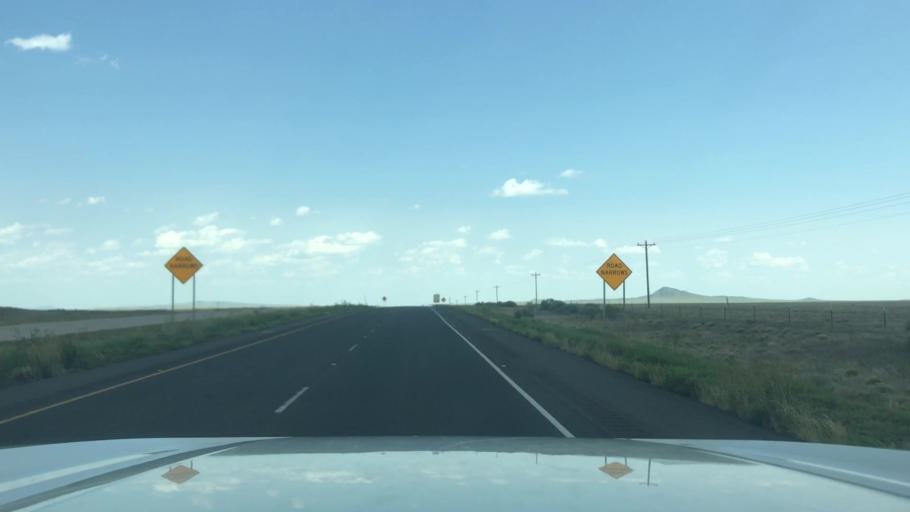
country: US
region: New Mexico
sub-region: Union County
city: Clayton
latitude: 36.6240
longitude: -103.7014
